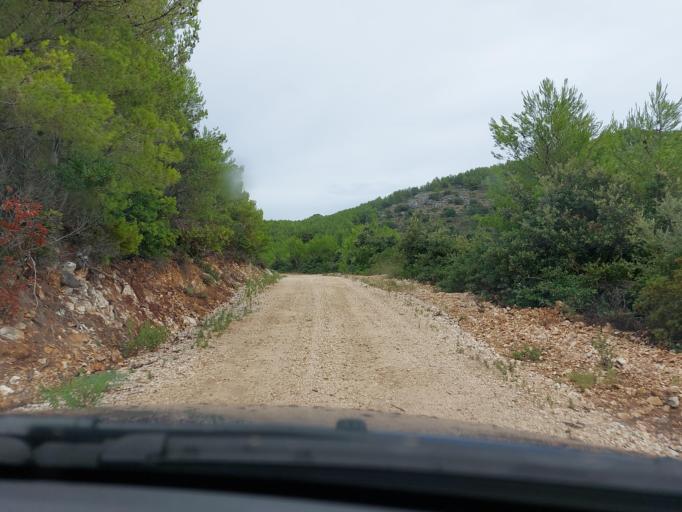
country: HR
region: Dubrovacko-Neretvanska
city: Smokvica
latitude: 42.7451
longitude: 16.9156
